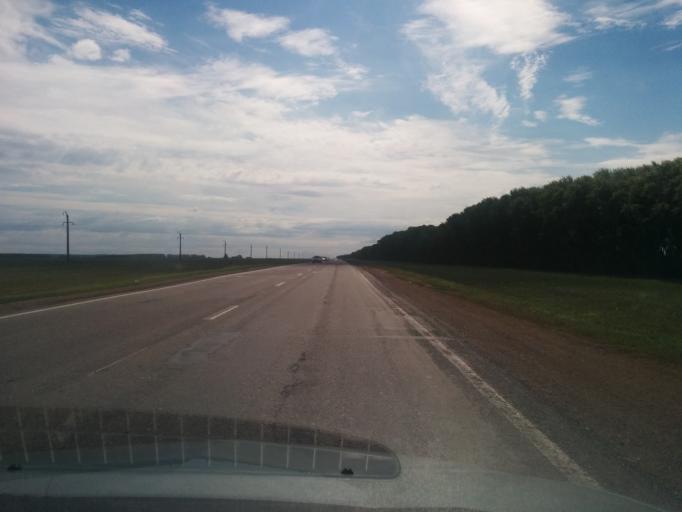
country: RU
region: Bashkortostan
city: Karmaskaly
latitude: 54.4196
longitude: 56.0464
